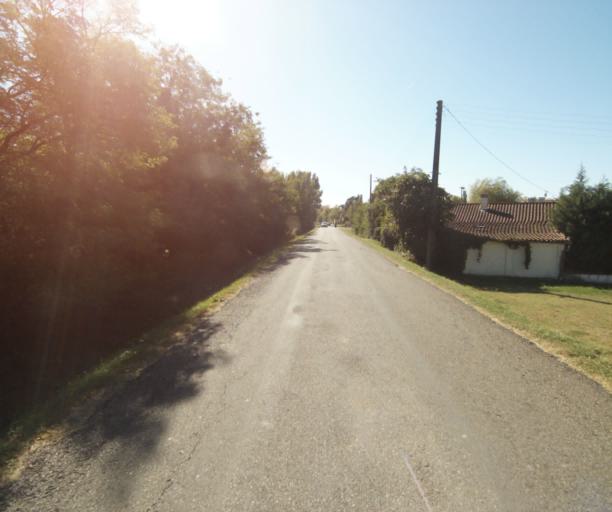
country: FR
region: Midi-Pyrenees
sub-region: Departement du Tarn-et-Garonne
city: Moissac
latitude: 44.1016
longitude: 1.1020
